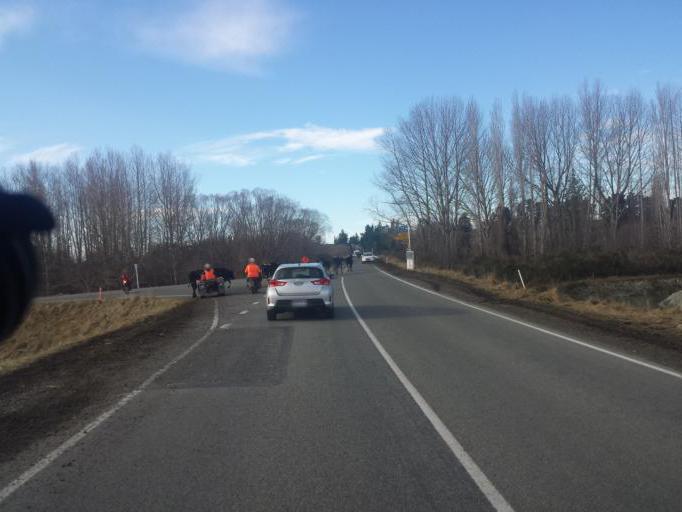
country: NZ
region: Canterbury
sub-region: Timaru District
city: Pleasant Point
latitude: -43.9754
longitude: 171.2974
